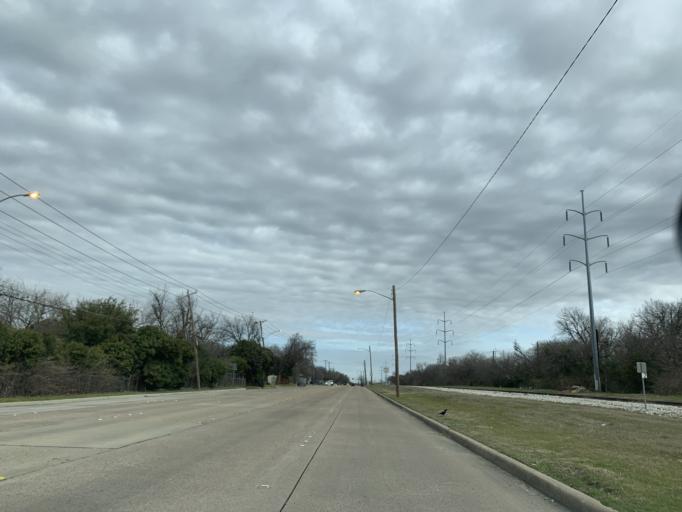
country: US
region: Texas
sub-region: Tarrant County
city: Edgecliff Village
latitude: 32.6858
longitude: -97.3697
